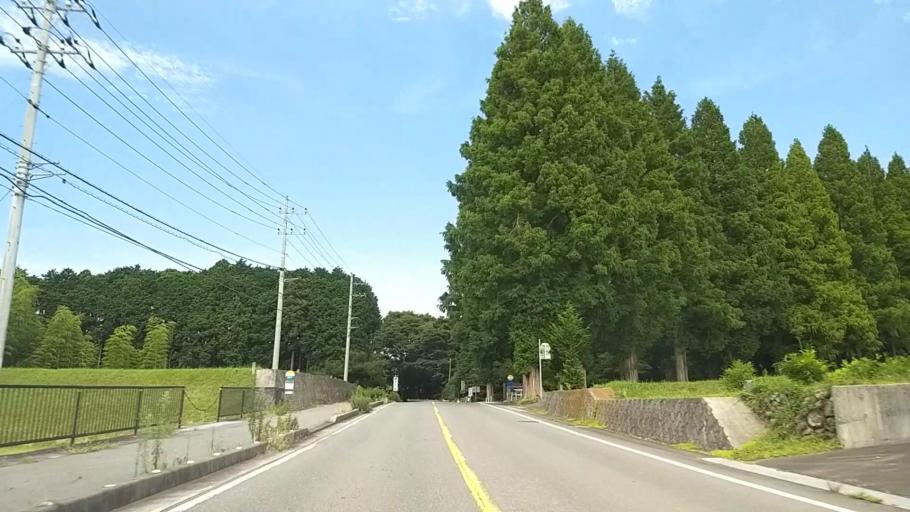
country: JP
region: Shizuoka
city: Gotemba
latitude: 35.2383
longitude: 138.8750
